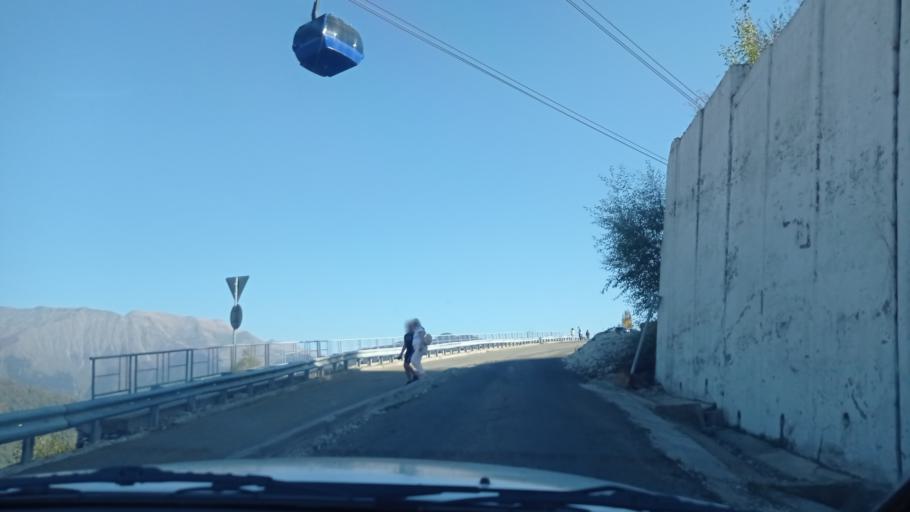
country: RU
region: Krasnodarskiy
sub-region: Sochi City
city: Krasnaya Polyana
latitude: 43.6611
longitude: 40.3232
